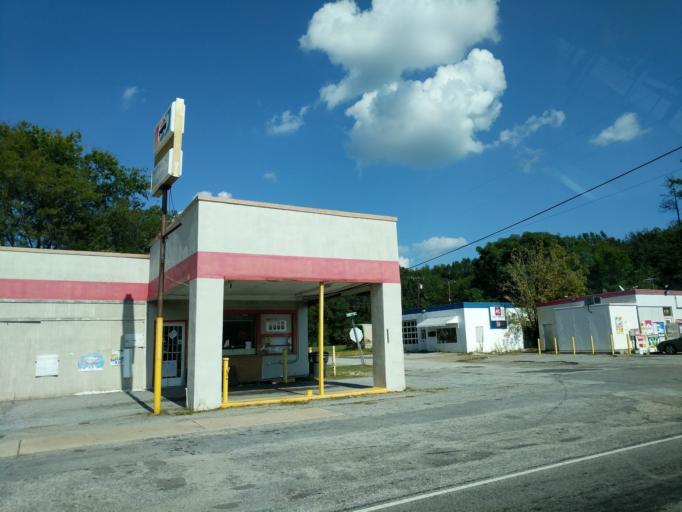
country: US
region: South Carolina
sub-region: Greenville County
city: Fountain Inn
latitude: 34.6085
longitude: -82.1142
